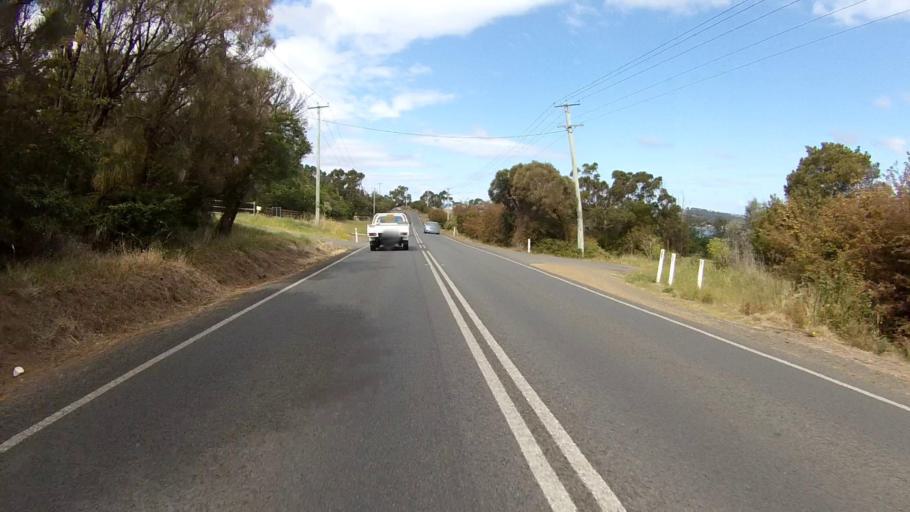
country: AU
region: Tasmania
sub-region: Clarence
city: Rokeby
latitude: -42.9067
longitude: 147.4649
